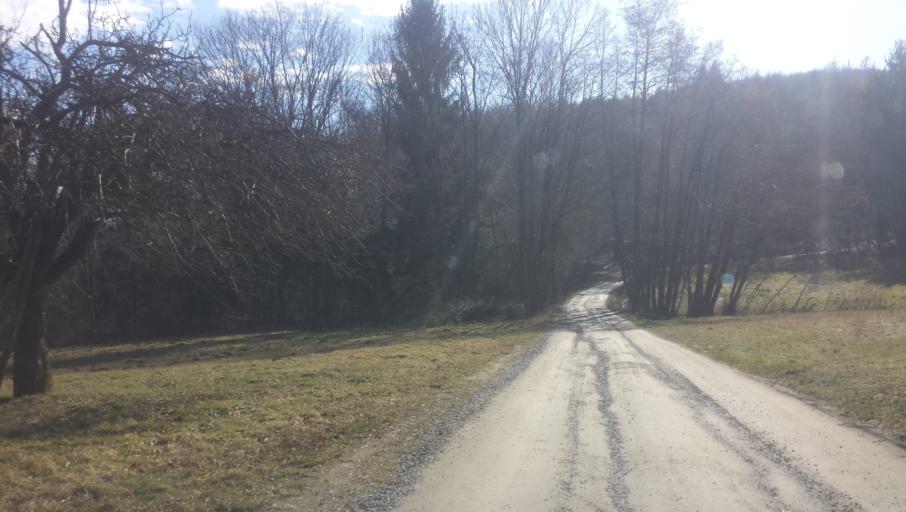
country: DE
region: Hesse
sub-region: Regierungsbezirk Darmstadt
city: Frankisch-Crumbach
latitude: 49.7460
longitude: 8.8218
